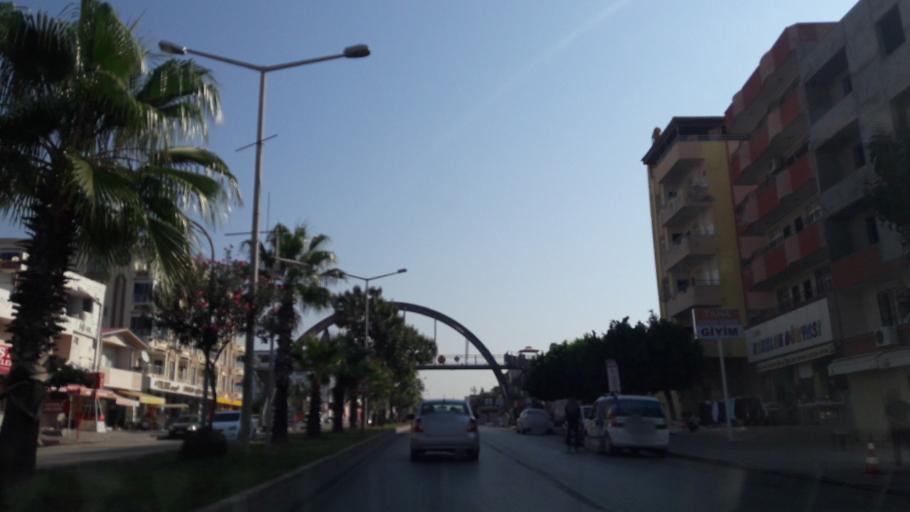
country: TR
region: Adana
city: Yuregir
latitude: 37.0377
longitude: 35.4220
